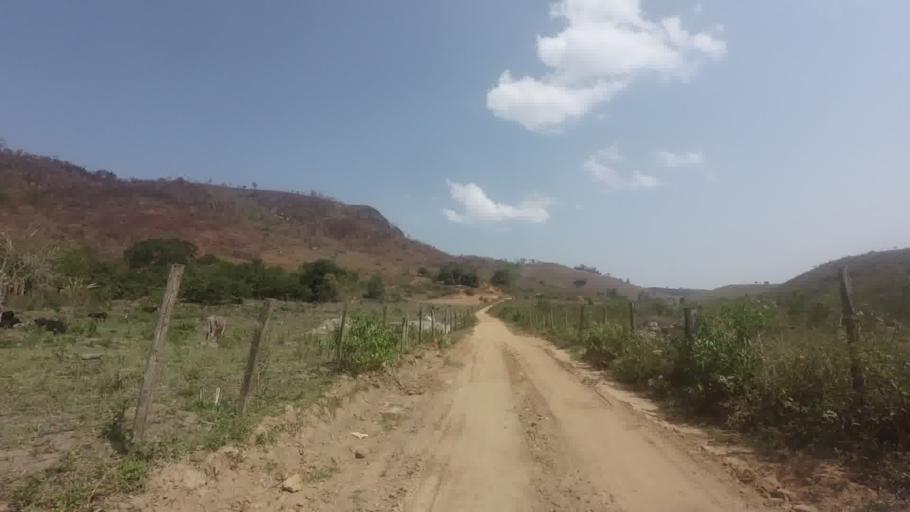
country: BR
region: Espirito Santo
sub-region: Sao Jose Do Calcado
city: Sao Jose do Calcado
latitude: -21.0278
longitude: -41.5168
